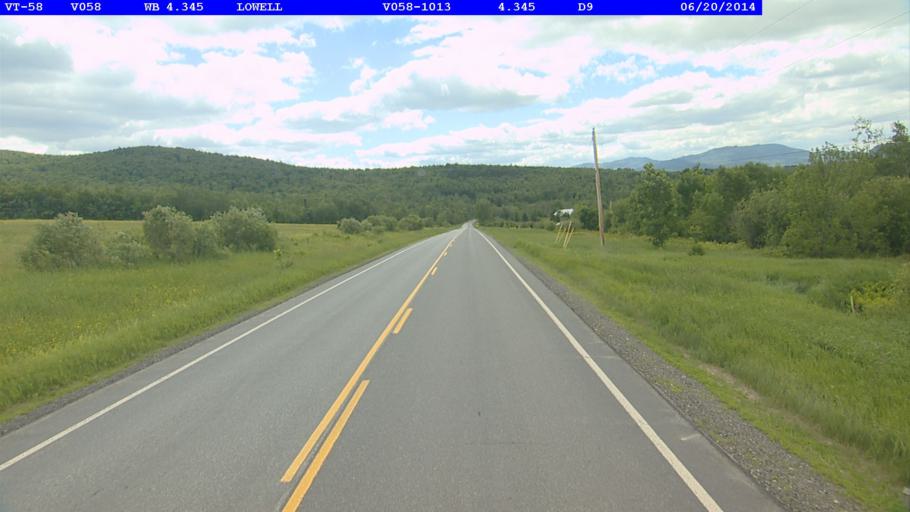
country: US
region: Vermont
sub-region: Orleans County
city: Newport
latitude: 44.8161
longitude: -72.3736
